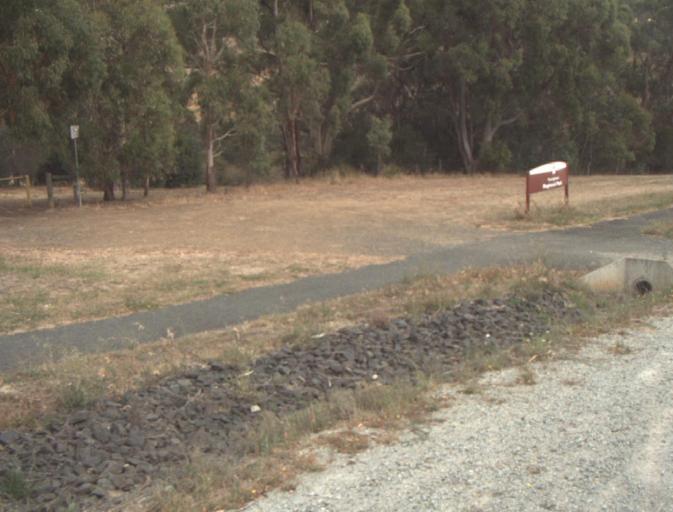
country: AU
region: Tasmania
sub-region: Launceston
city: Newstead
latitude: -41.4766
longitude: 147.1818
